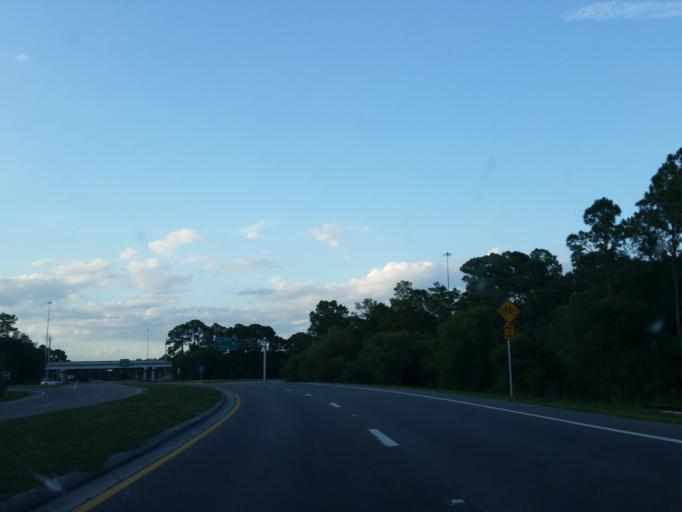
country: US
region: Florida
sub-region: Sarasota County
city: North Port
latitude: 27.0965
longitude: -82.2034
